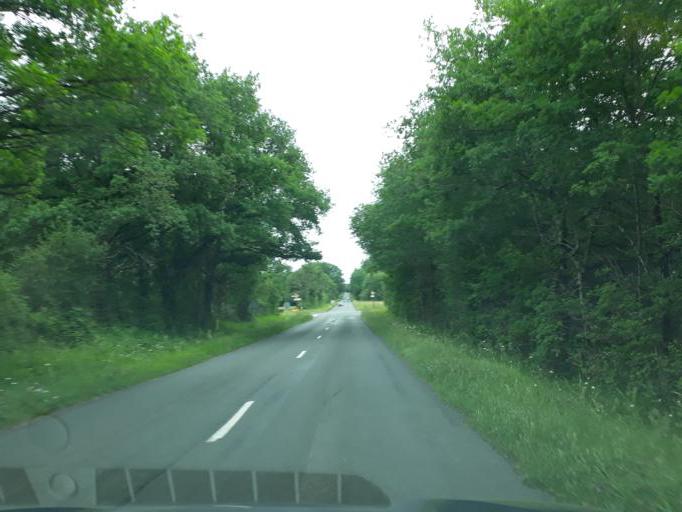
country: FR
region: Centre
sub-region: Departement du Loiret
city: Saint-Pere-sur-Loire
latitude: 47.7310
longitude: 2.3475
